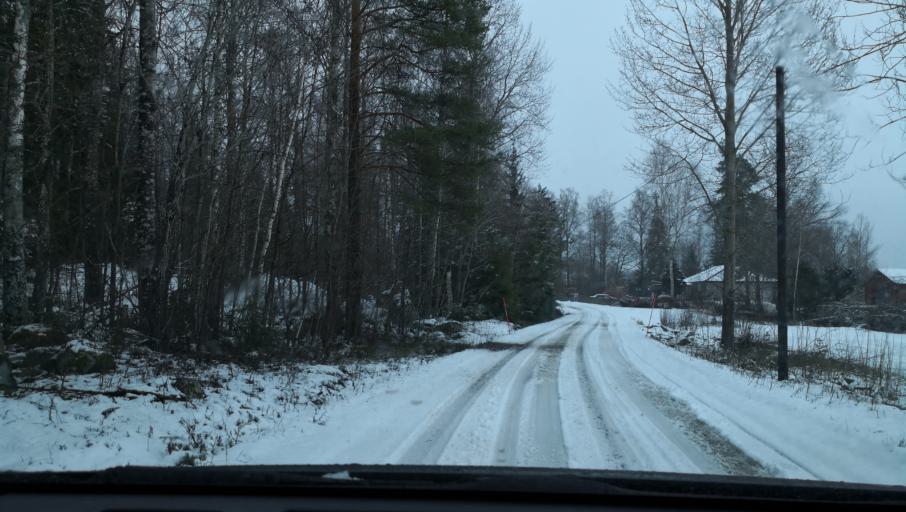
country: SE
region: Vaestmanland
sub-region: Kopings Kommun
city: Kolsva
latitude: 59.5648
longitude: 15.7852
